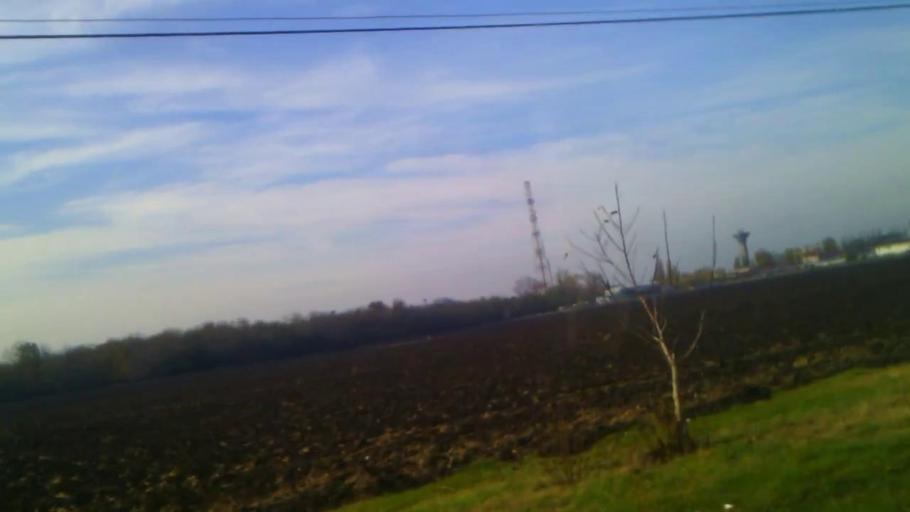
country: RO
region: Ilfov
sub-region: Comuna Berceni
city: Berceni
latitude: 44.3369
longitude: 26.1676
